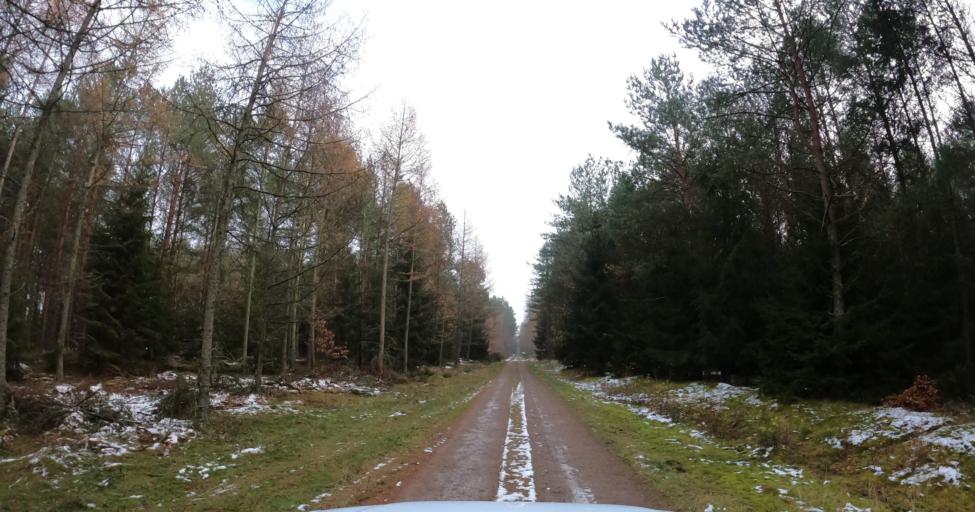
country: PL
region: West Pomeranian Voivodeship
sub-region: Powiat swidwinski
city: Rabino
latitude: 53.9007
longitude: 15.8953
